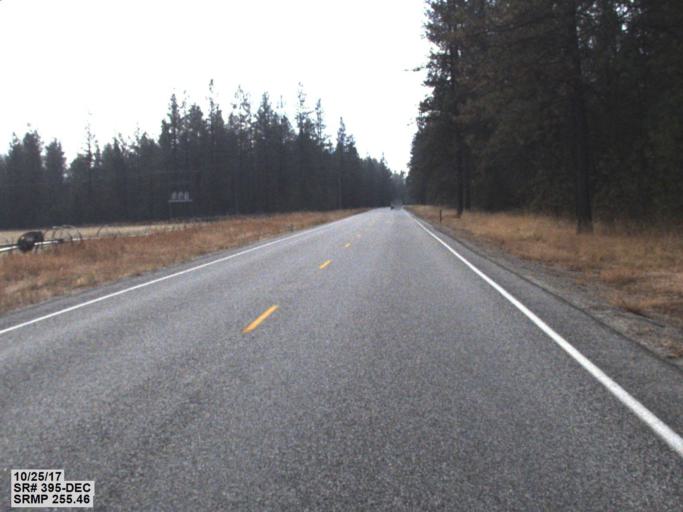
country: US
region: Washington
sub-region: Stevens County
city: Kettle Falls
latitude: 48.8080
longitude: -118.1641
